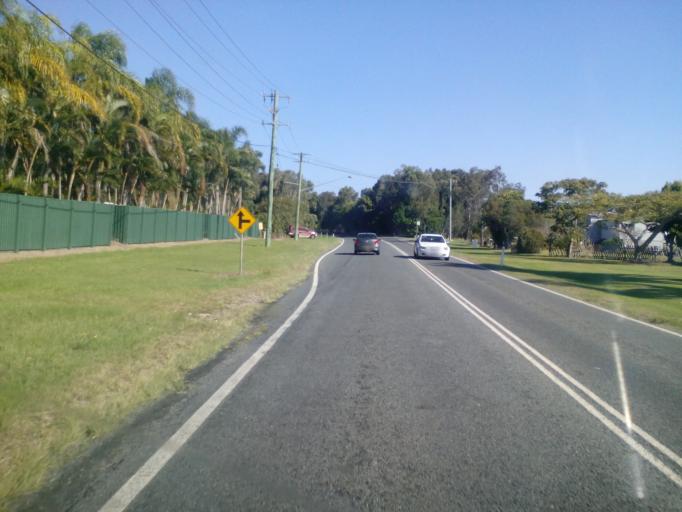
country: AU
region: New South Wales
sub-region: Tweed
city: Kingscliff
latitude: -28.2558
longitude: 153.5598
